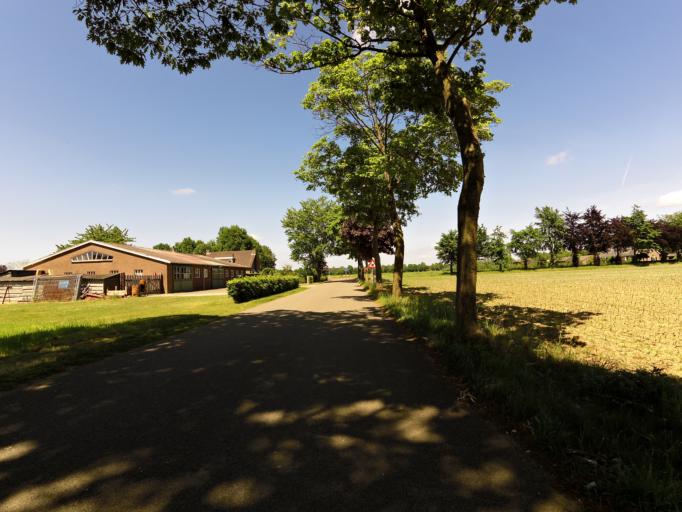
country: NL
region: Gelderland
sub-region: Gemeente Bronckhorst
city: Hengelo
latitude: 52.0694
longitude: 6.2931
